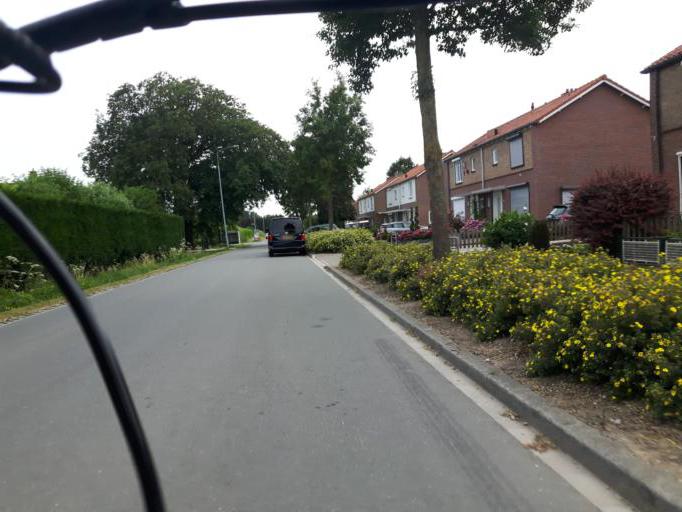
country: NL
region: Gelderland
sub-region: Gemeente Tiel
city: Tiel
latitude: 51.8734
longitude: 5.3733
